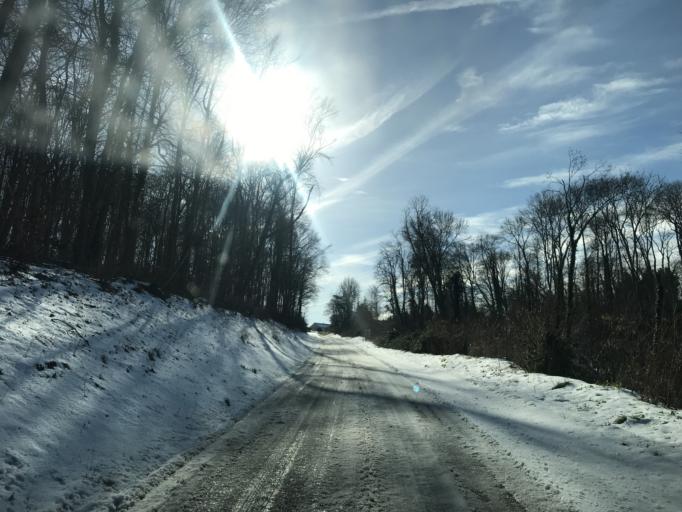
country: FR
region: Haute-Normandie
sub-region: Departement de l'Eure
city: Gravigny
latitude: 49.0790
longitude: 1.2581
